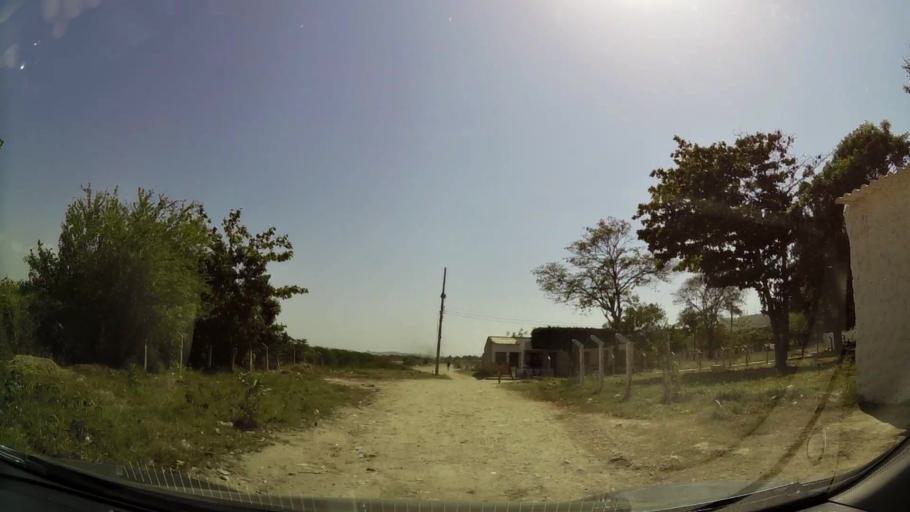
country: CO
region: Bolivar
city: Cartagena
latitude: 10.4338
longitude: -75.5143
